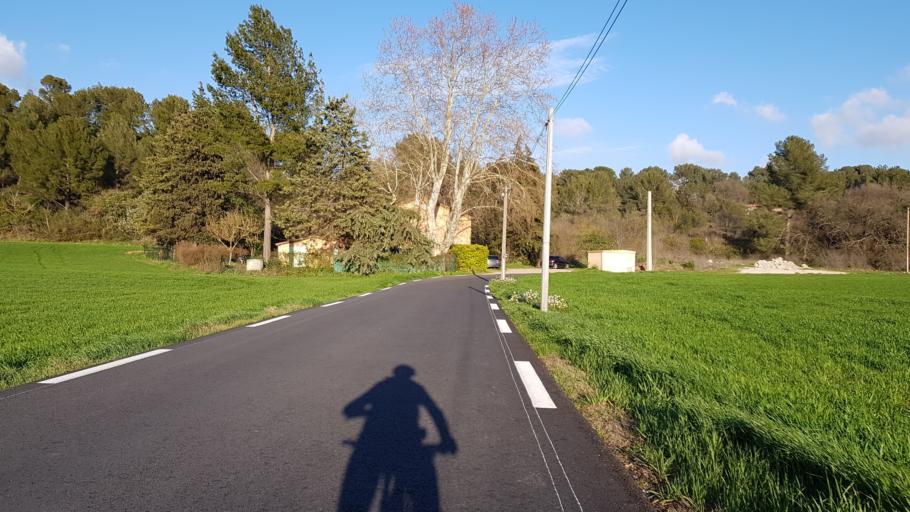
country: FR
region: Provence-Alpes-Cote d'Azur
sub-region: Departement des Bouches-du-Rhone
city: Bouc-Bel-Air
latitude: 43.5007
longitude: 5.4043
